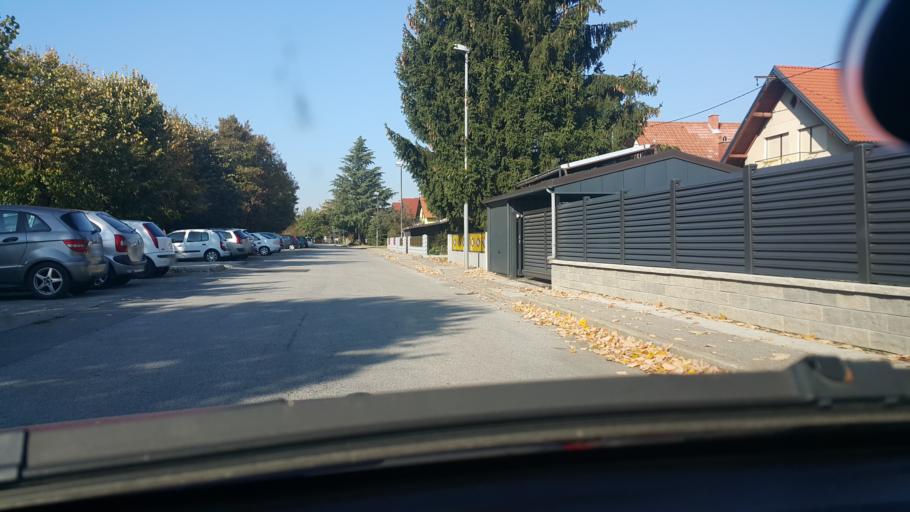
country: SI
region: Miklavz na Dravskem Polju
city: Miklavz na Dravskem Polju
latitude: 46.5277
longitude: 15.6877
